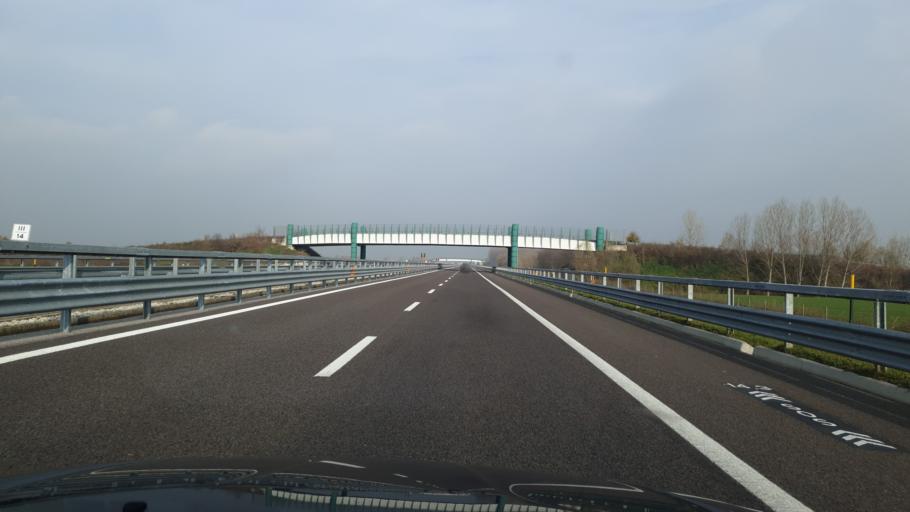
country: IT
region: Veneto
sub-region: Provincia di Padova
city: Megliadino San Vitale
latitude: 45.1836
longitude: 11.5387
